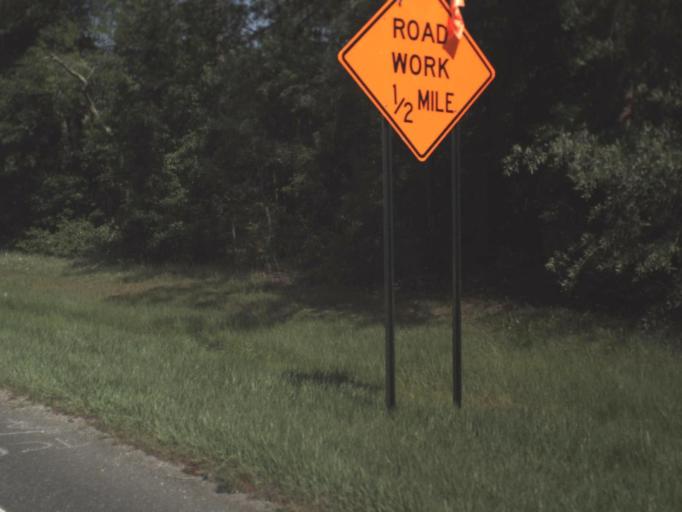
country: US
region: Florida
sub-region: Clay County
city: Green Cove Springs
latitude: 29.9834
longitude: -81.7452
